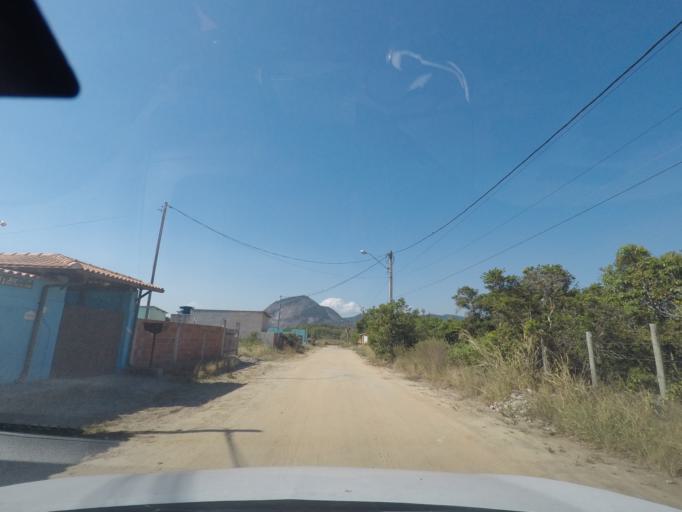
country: BR
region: Rio de Janeiro
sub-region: Marica
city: Marica
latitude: -22.9661
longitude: -42.9074
